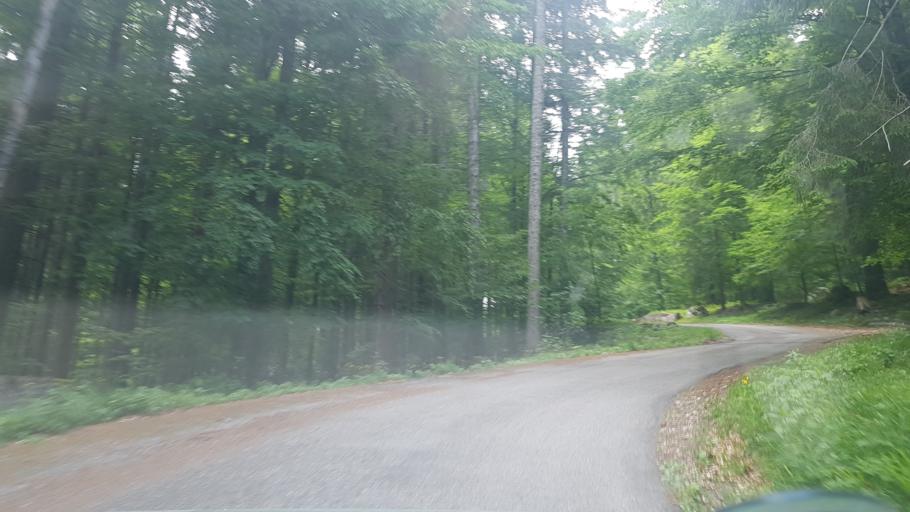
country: IT
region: Friuli Venezia Giulia
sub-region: Provincia di Udine
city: Paularo
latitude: 46.5348
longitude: 13.2089
